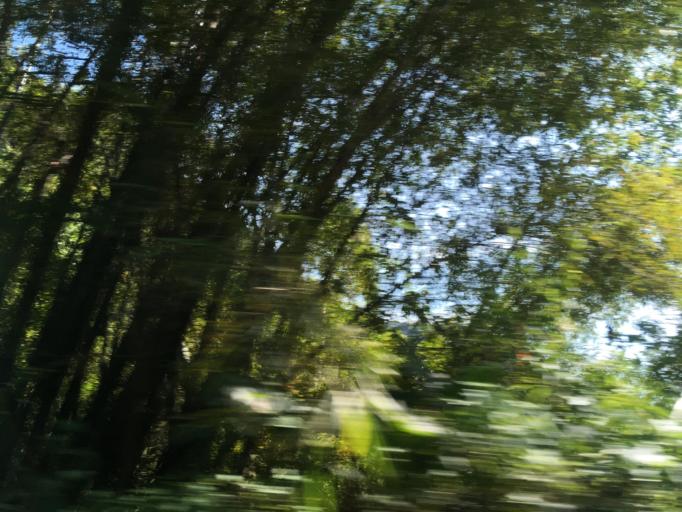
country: TW
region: Taiwan
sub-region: Yilan
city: Yilan
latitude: 24.4381
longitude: 121.7532
